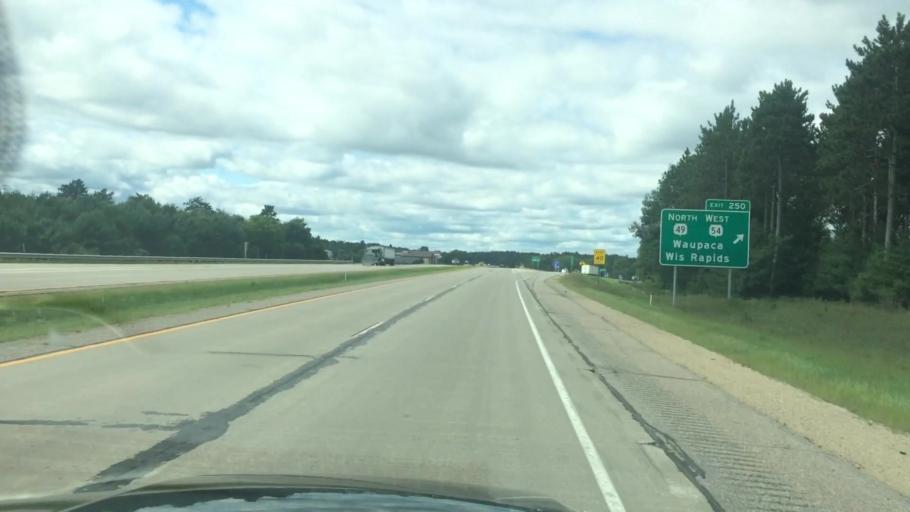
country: US
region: Wisconsin
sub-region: Waupaca County
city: Waupaca
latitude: 44.3530
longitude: -89.1109
